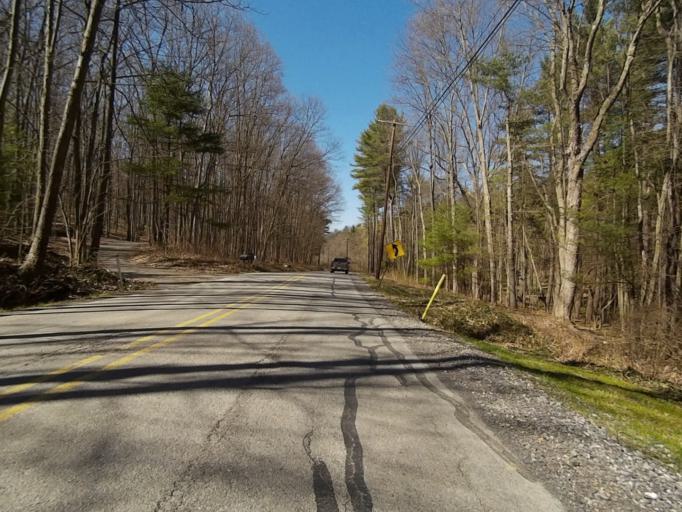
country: US
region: Pennsylvania
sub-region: Centre County
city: Stormstown
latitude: 40.7485
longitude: -78.0314
